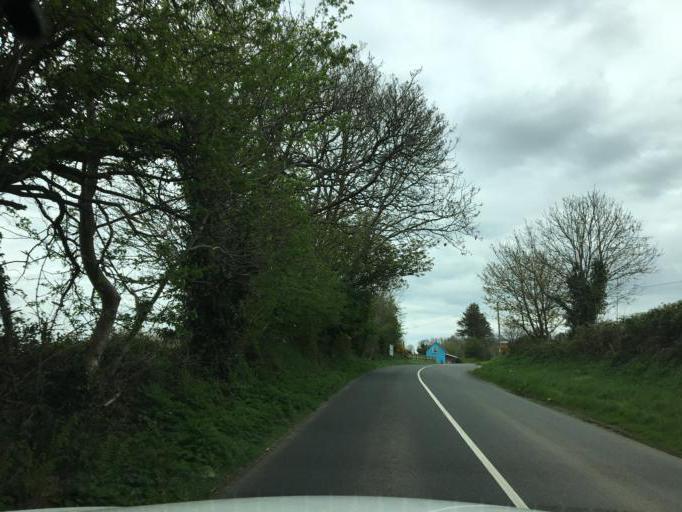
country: IE
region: Leinster
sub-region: Loch Garman
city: Enniscorthy
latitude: 52.4158
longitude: -6.6198
